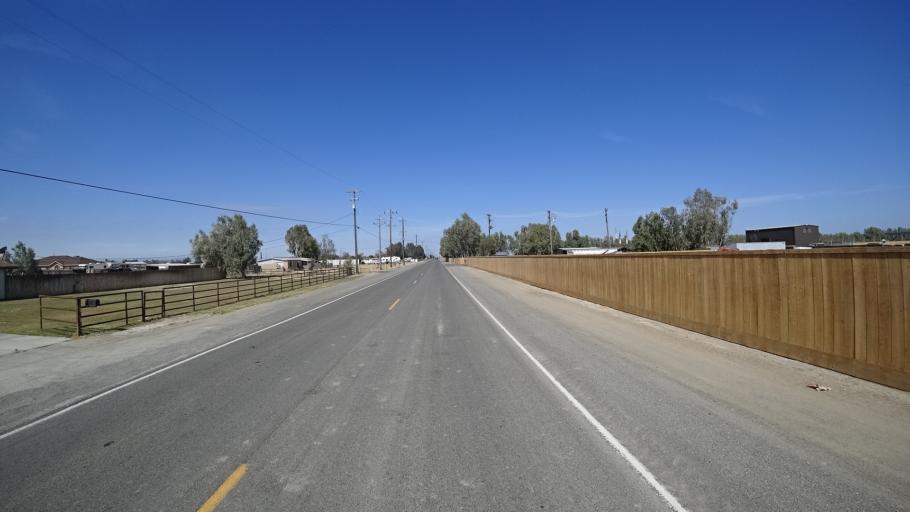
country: US
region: California
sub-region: Kings County
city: Lemoore
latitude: 36.2546
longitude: -119.7891
